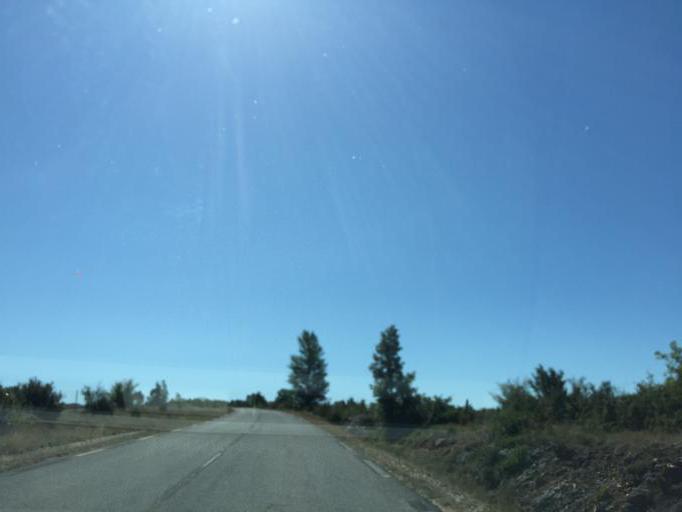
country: FR
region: Midi-Pyrenees
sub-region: Departement de l'Aveyron
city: La Cavalerie
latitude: 43.9243
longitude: 3.2393
